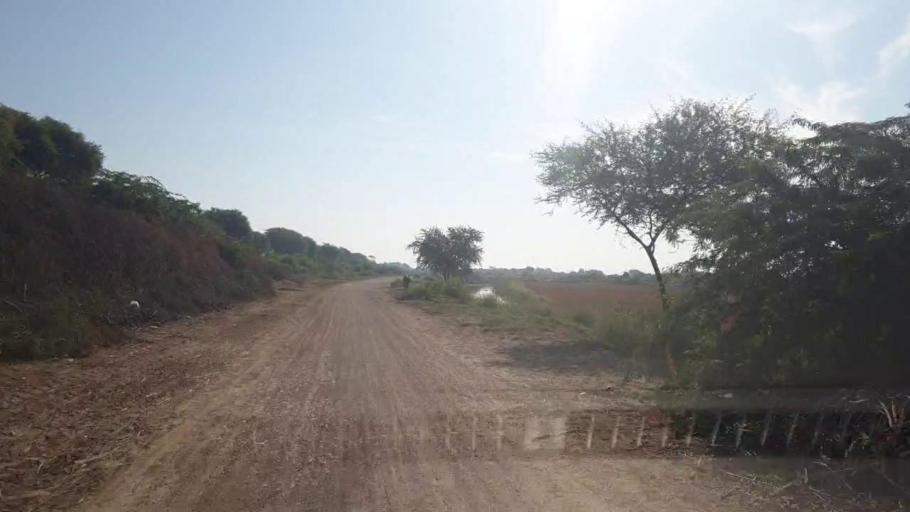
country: PK
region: Sindh
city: Rajo Khanani
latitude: 24.9705
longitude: 68.7924
